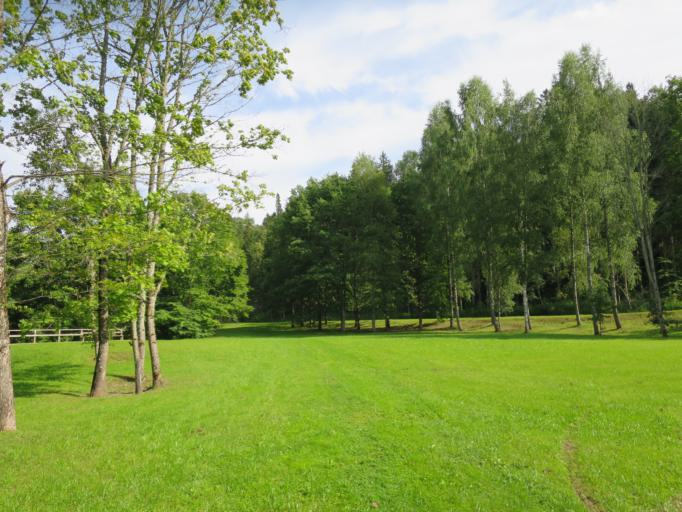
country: LV
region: Ligatne
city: Ligatne
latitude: 57.2317
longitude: 25.0437
